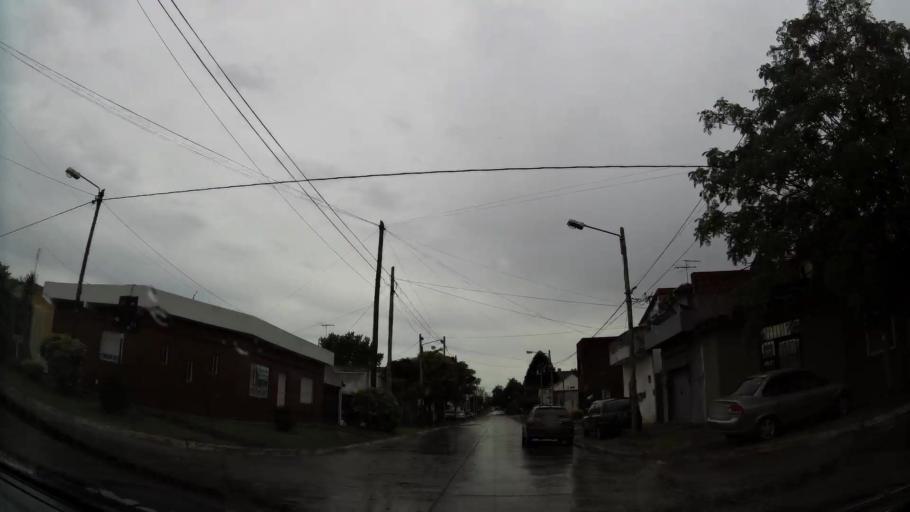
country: AR
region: Buenos Aires
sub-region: Partido de Quilmes
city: Quilmes
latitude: -34.7659
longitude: -58.2279
